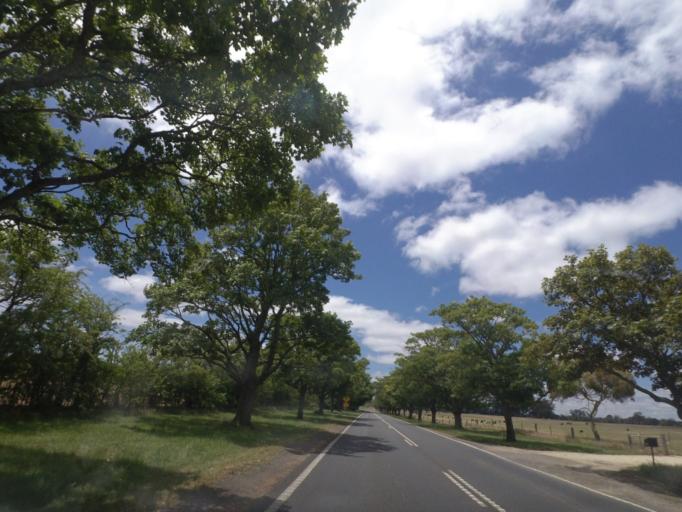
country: AU
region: Victoria
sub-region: Mount Alexander
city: Castlemaine
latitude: -37.3370
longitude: 144.1621
